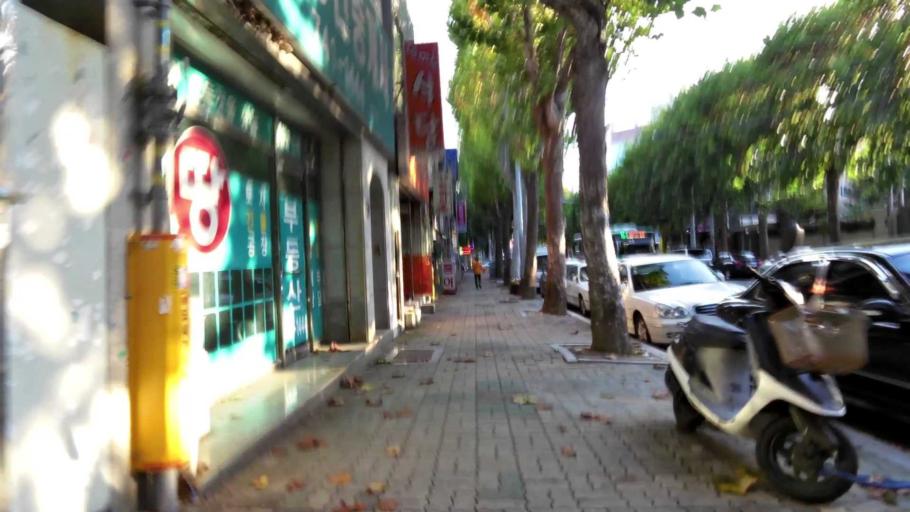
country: KR
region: Daegu
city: Daegu
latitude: 35.8604
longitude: 128.6402
